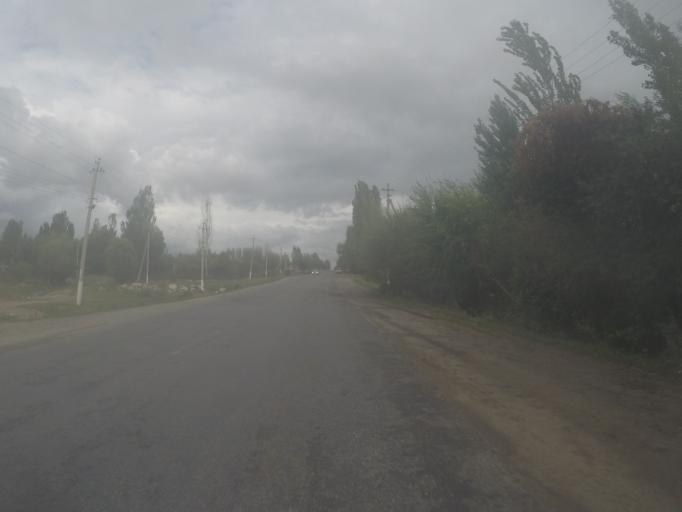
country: KG
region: Ysyk-Koel
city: Tyup
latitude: 42.7476
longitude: 78.0910
